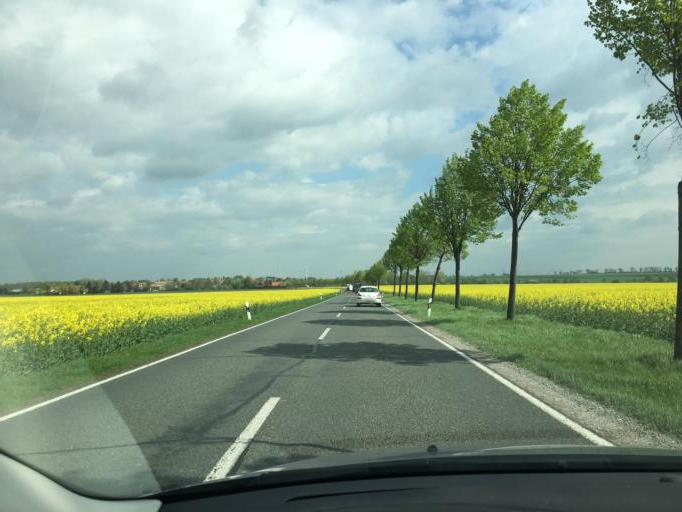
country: DE
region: Saxony-Anhalt
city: Giersleben
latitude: 51.7274
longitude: 11.5882
